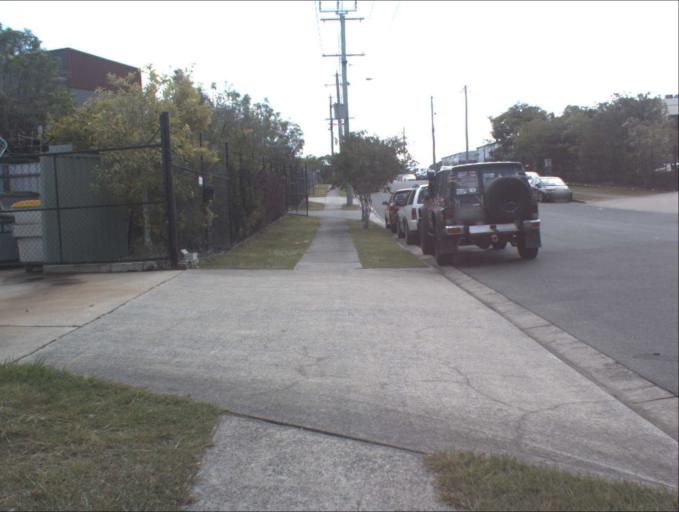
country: AU
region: Queensland
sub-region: Logan
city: Slacks Creek
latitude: -27.6669
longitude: 153.1343
